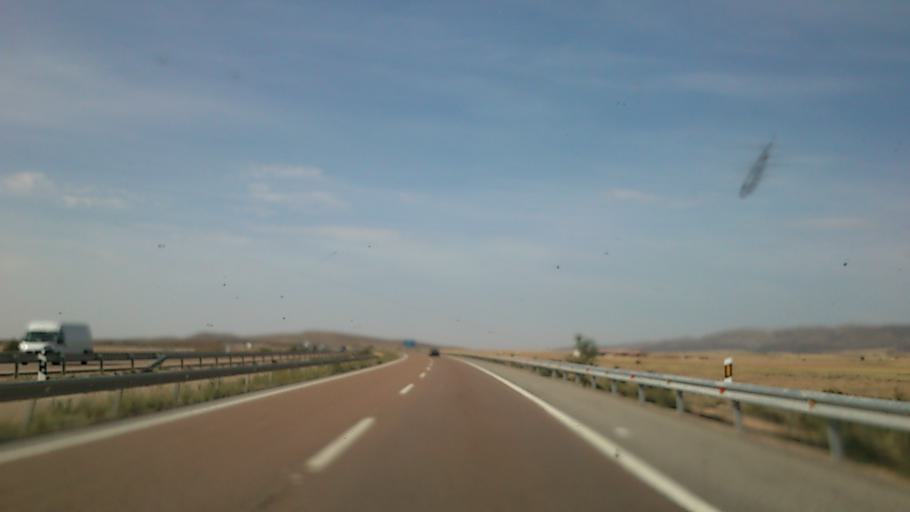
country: ES
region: Aragon
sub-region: Provincia de Teruel
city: Santa Eulalia
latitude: 40.6056
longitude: -1.2859
